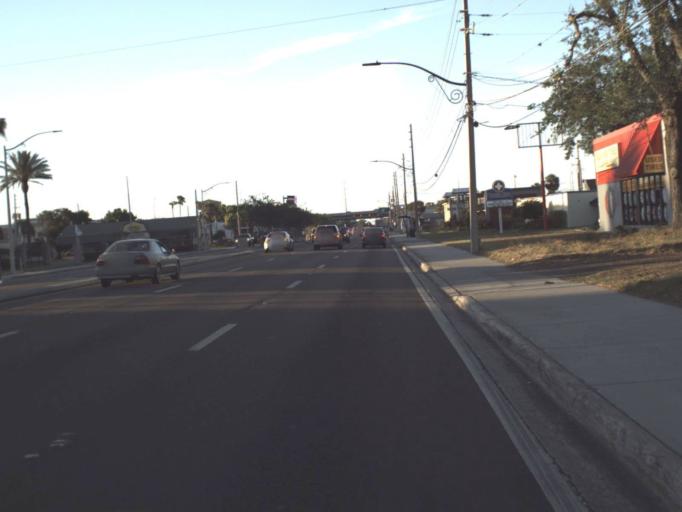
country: US
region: Florida
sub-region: Orange County
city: Azalea Park
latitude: 28.5355
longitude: -81.3104
